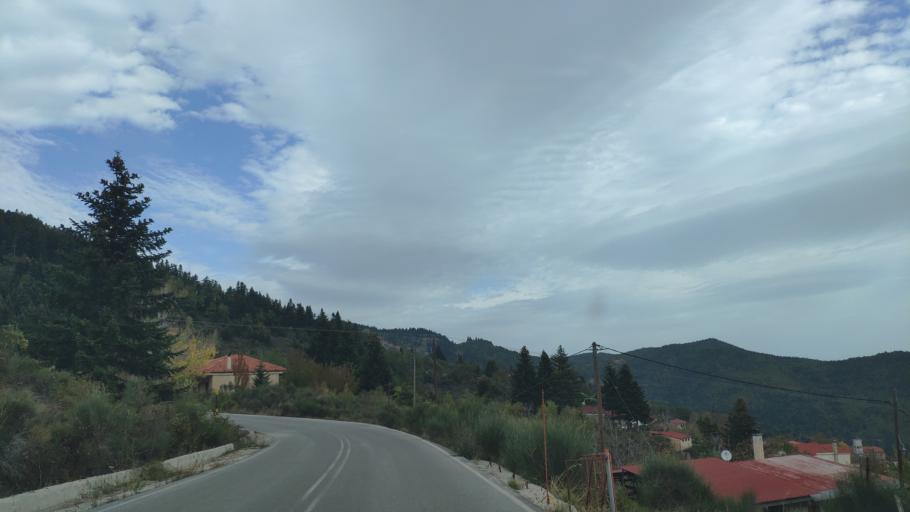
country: GR
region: Central Greece
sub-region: Nomos Fokidos
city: Amfissa
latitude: 38.6853
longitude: 22.3197
